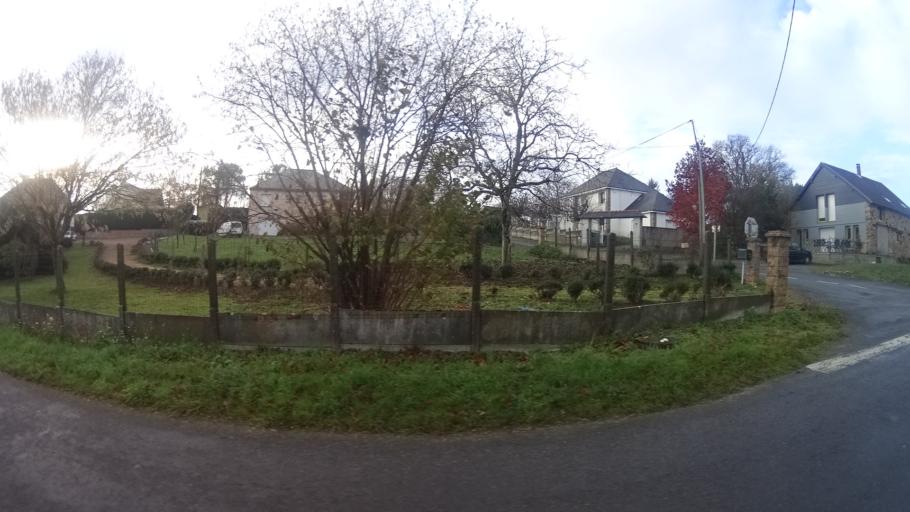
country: FR
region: Pays de la Loire
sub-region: Departement de la Loire-Atlantique
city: Avessac
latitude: 47.6507
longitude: -1.9845
